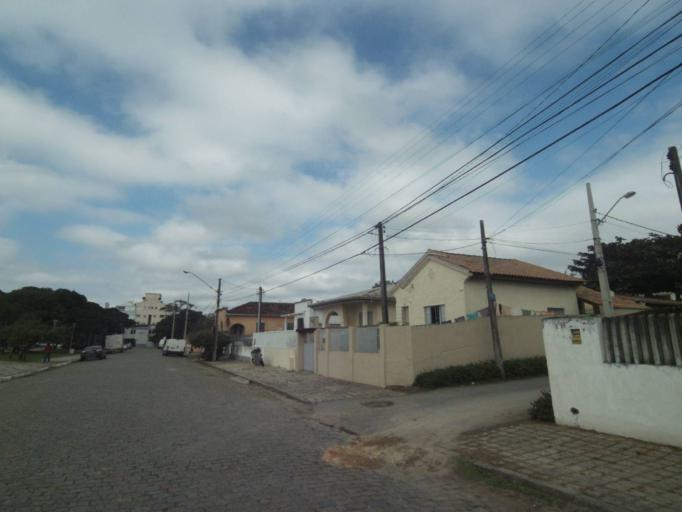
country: BR
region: Parana
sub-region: Paranagua
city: Paranagua
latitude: -25.5218
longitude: -48.5145
